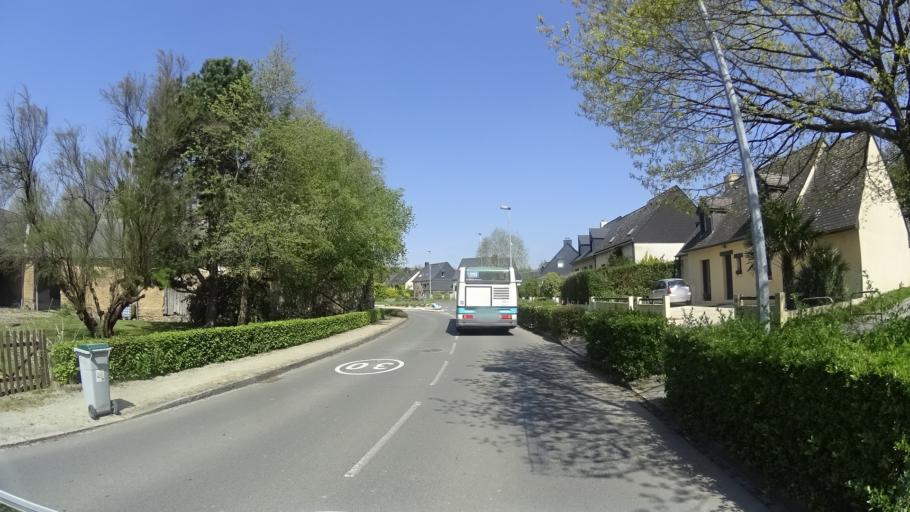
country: FR
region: Brittany
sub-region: Departement d'Ille-et-Vilaine
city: Chavagne
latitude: 48.0571
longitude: -1.7884
